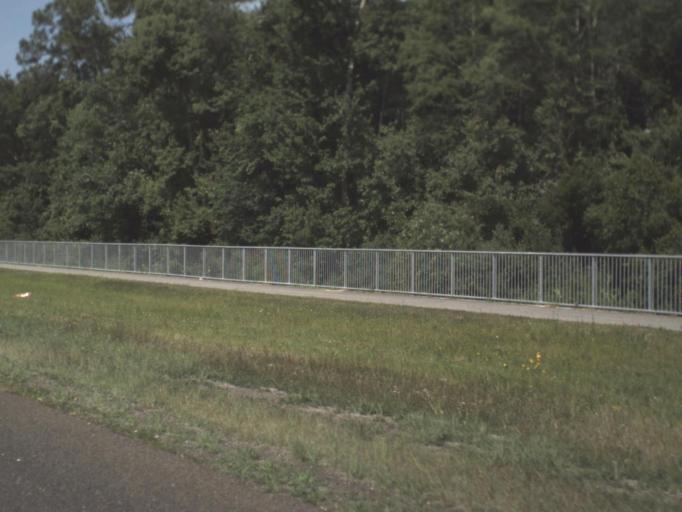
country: US
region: Florida
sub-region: Saint Johns County
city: Saint Augustine Shores
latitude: 29.7976
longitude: -81.4144
